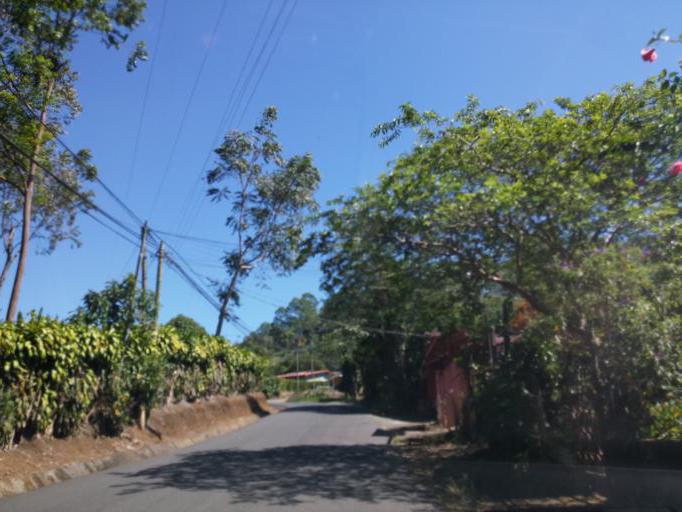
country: CR
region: San Jose
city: Palmichal
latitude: 9.8383
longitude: -84.2083
